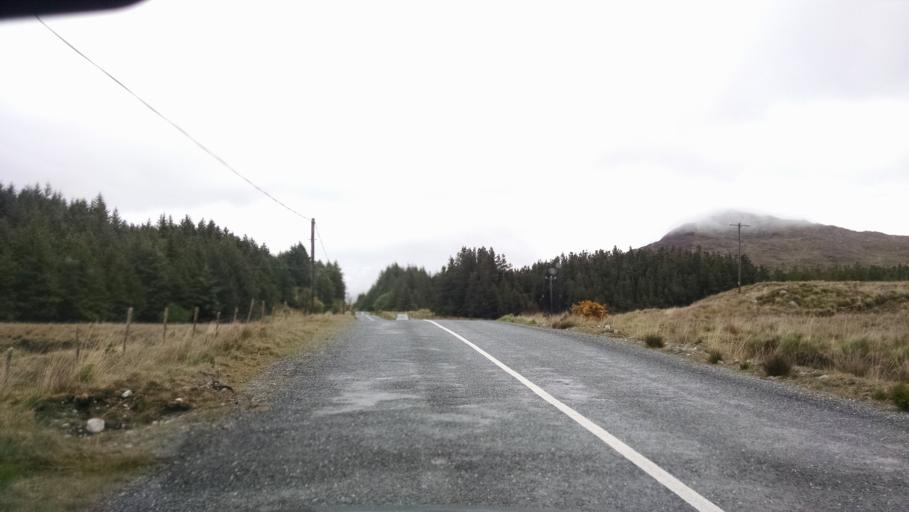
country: IE
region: Connaught
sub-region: County Galway
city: Clifden
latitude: 53.4697
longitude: -9.7486
